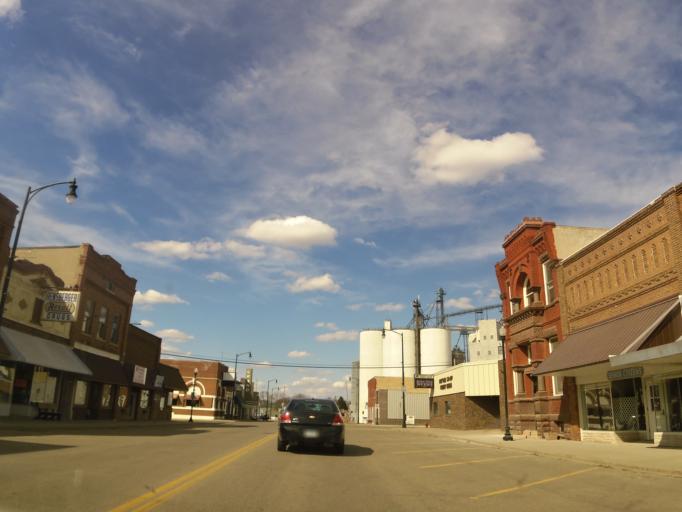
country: US
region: Minnesota
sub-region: Lac qui Parle County
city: Dawson
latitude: 44.9293
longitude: -96.0547
